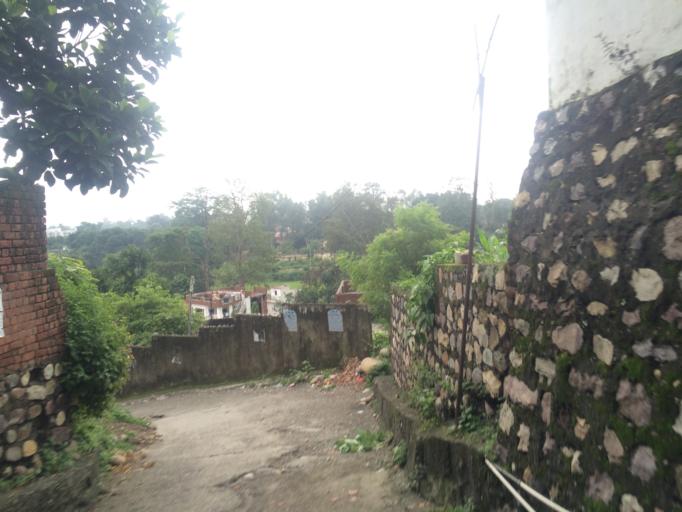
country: IN
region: Uttarakhand
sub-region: Dehradun
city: Birbhaddar
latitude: 30.0745
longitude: 78.2781
